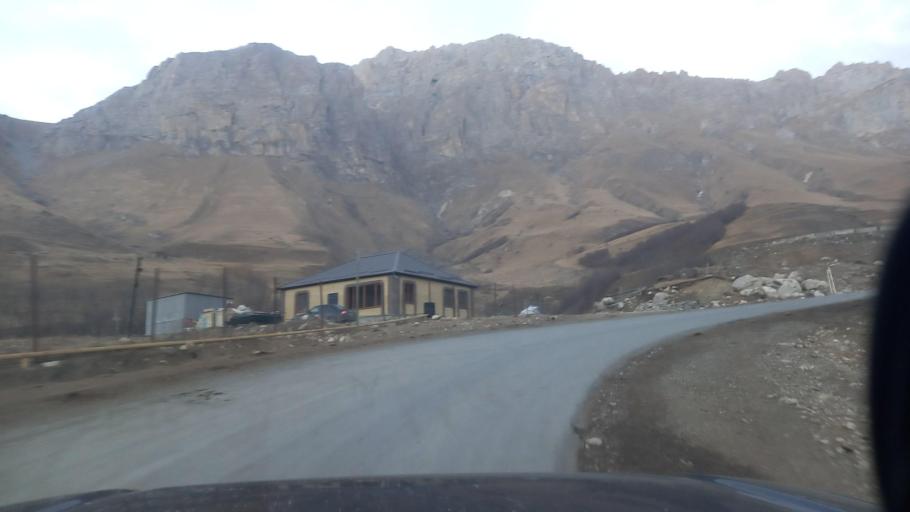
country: RU
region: Ingushetiya
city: Dzhayrakh
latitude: 42.8207
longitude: 44.8157
